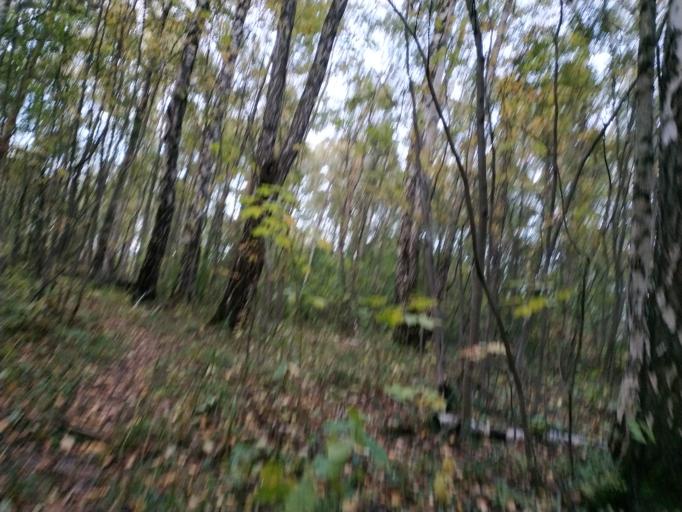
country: RU
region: Moscow
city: Khimki
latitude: 55.8737
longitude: 37.4328
